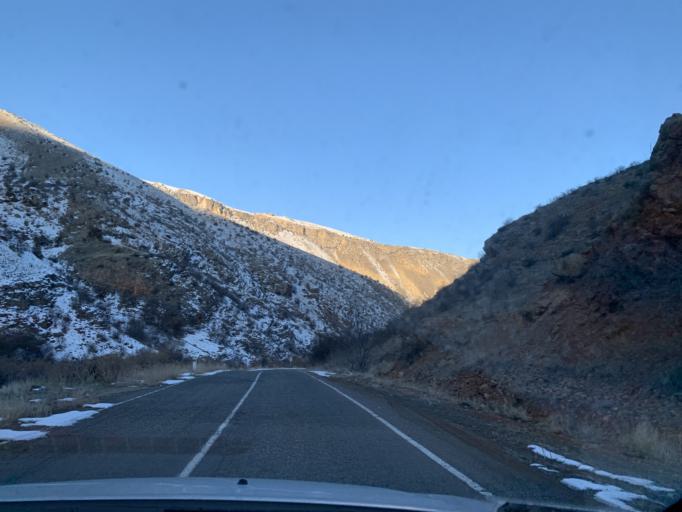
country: AM
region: Vayots' Dzori Marz
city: Areni
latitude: 39.6908
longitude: 45.2196
